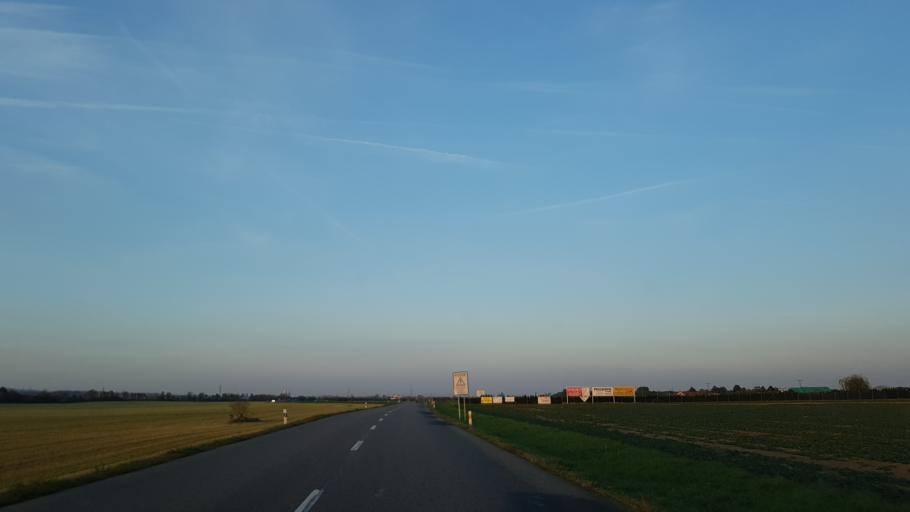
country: CZ
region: Zlin
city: Nedakonice
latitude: 49.0435
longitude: 17.3926
